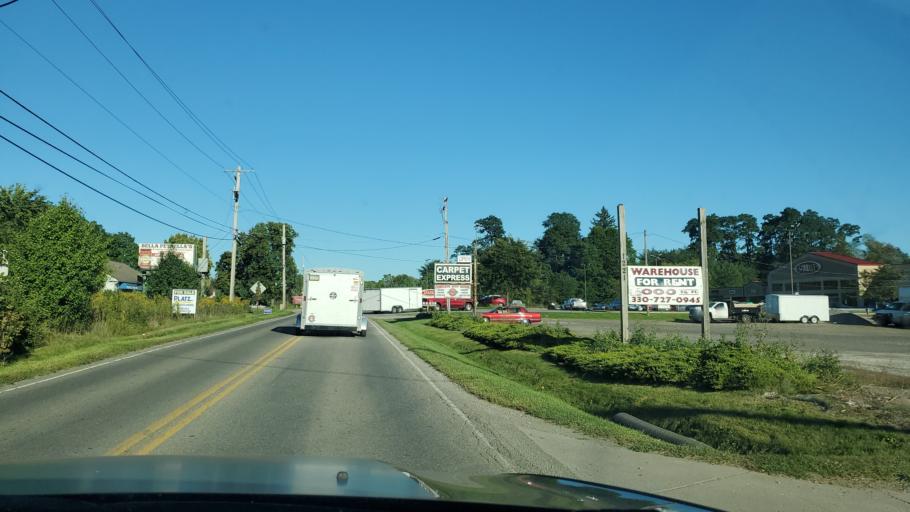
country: US
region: Ohio
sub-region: Mahoning County
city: Boardman
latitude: 40.9879
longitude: -80.6734
